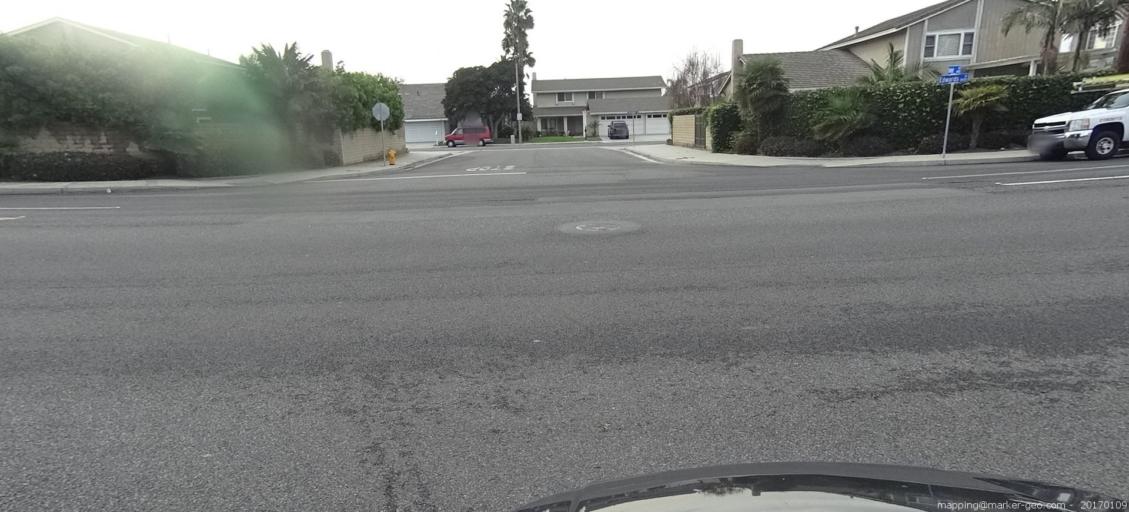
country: US
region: California
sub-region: Orange County
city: Huntington Beach
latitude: 33.6992
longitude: -118.0149
